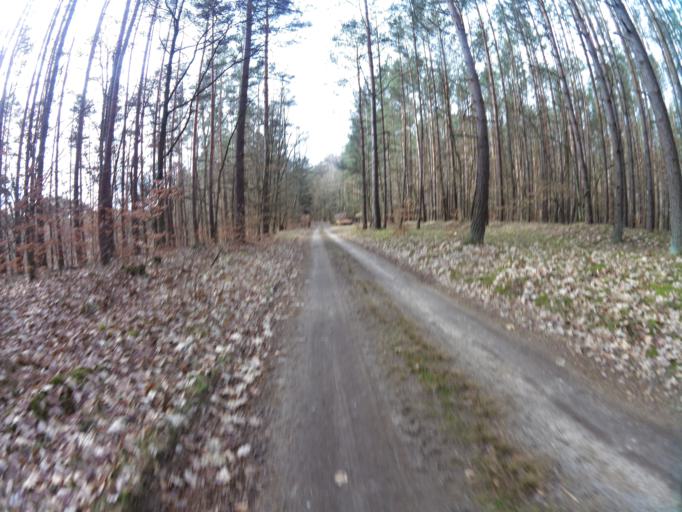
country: PL
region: West Pomeranian Voivodeship
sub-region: Powiat mysliborski
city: Mysliborz
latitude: 52.8648
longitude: 14.8490
